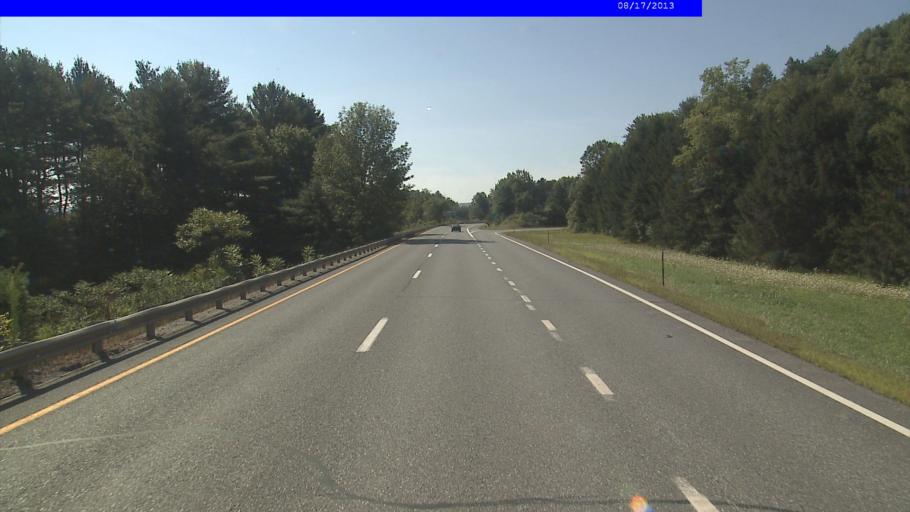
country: US
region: New Hampshire
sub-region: Sullivan County
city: Charlestown
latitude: 43.2692
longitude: -72.4338
